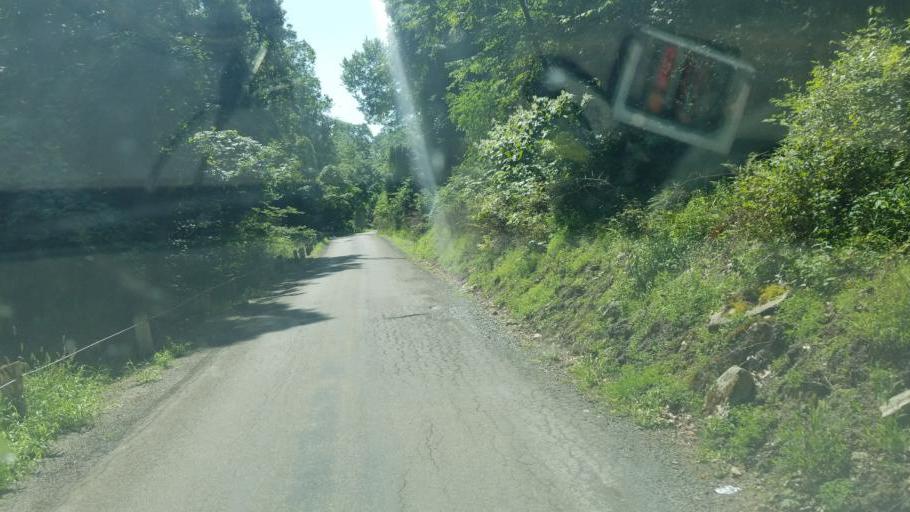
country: US
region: Pennsylvania
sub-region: Clarion County
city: Clarion
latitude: 41.1828
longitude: -79.4325
